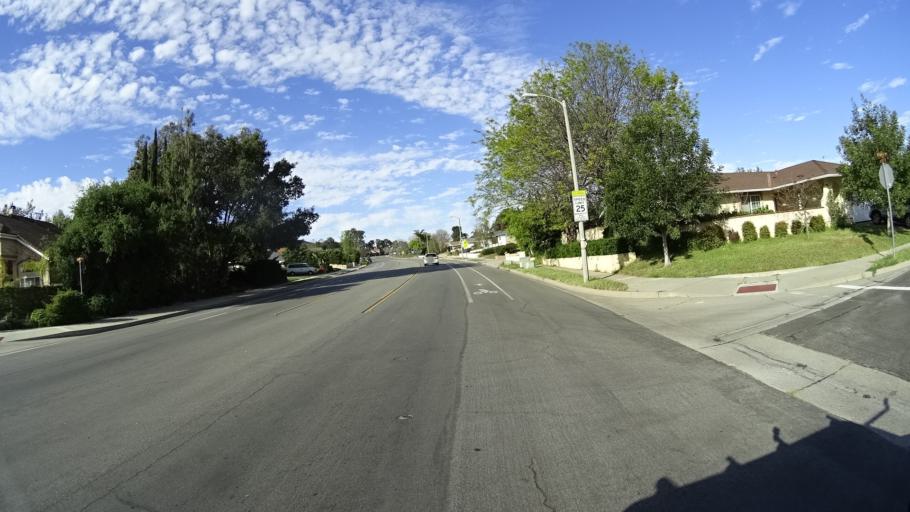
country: US
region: California
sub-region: Ventura County
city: Casa Conejo
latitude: 34.1750
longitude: -118.9482
